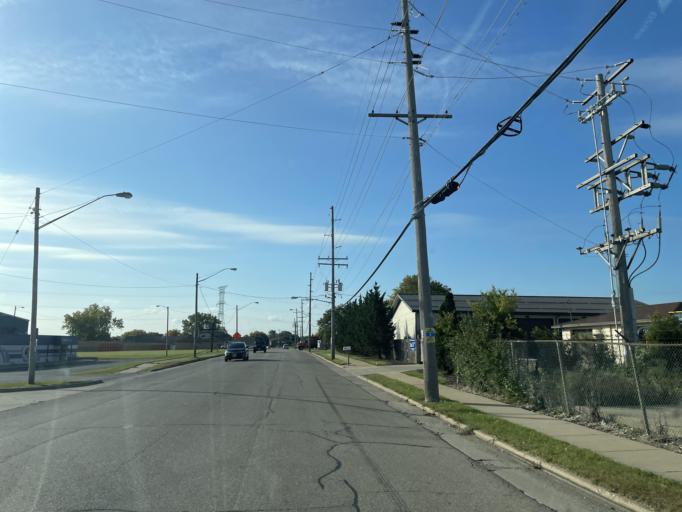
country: US
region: Wisconsin
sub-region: Kenosha County
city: Pleasant Prairie
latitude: 42.5638
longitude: -87.8803
